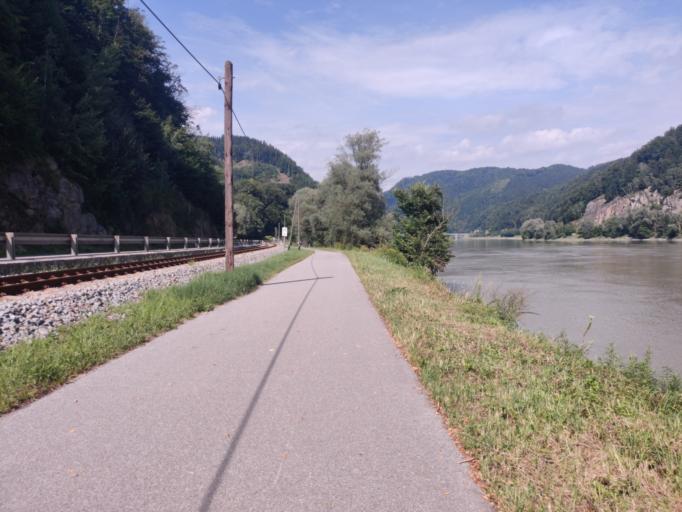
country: AT
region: Upper Austria
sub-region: Politischer Bezirk Perg
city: Bad Kreuzen
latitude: 48.2005
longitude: 14.8456
